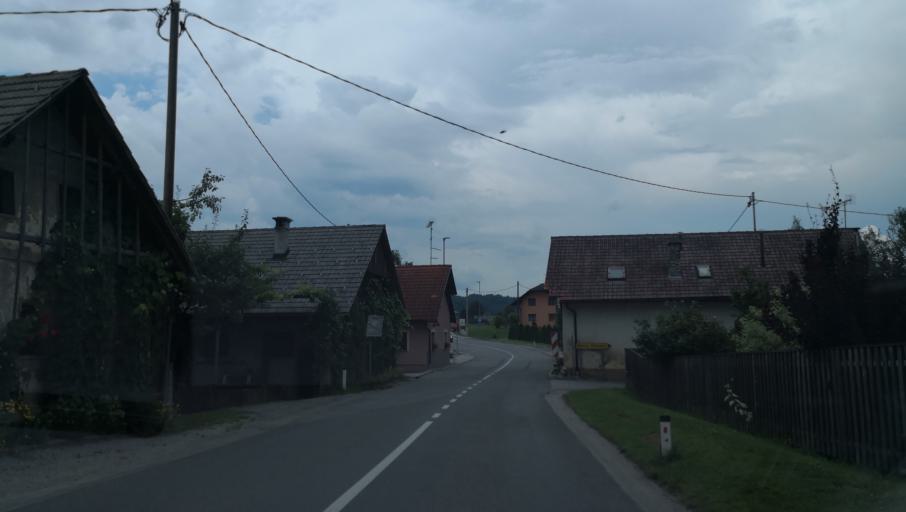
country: SI
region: Ivancna Gorica
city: Ivancna Gorica
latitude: 45.8706
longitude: 14.8190
